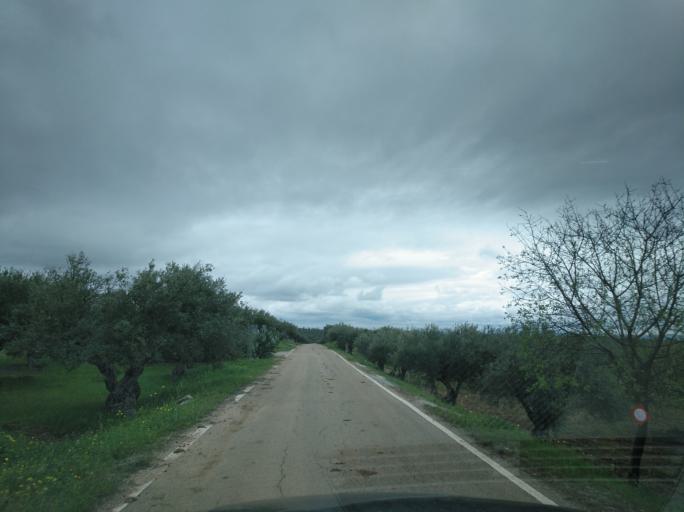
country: PT
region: Portalegre
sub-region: Campo Maior
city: Campo Maior
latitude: 38.9842
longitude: -7.0371
